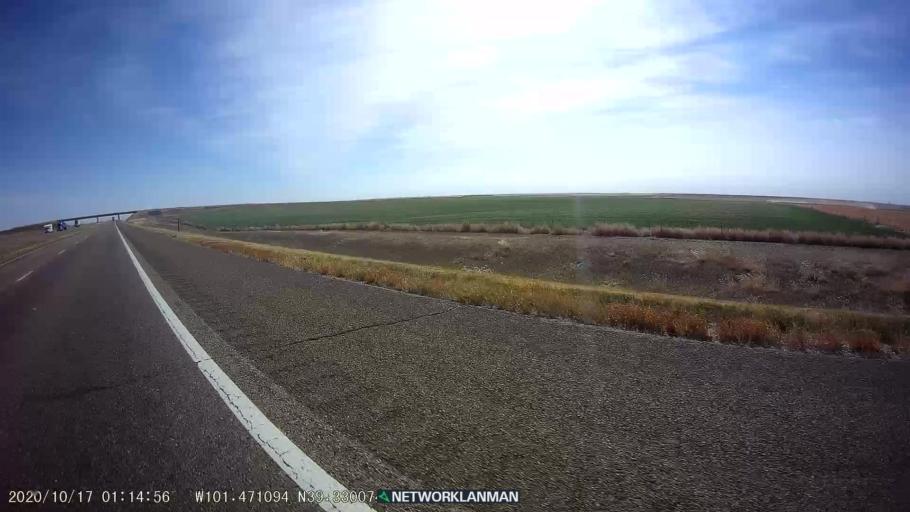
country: US
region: Kansas
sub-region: Sherman County
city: Goodland
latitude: 39.3298
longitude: -101.4707
